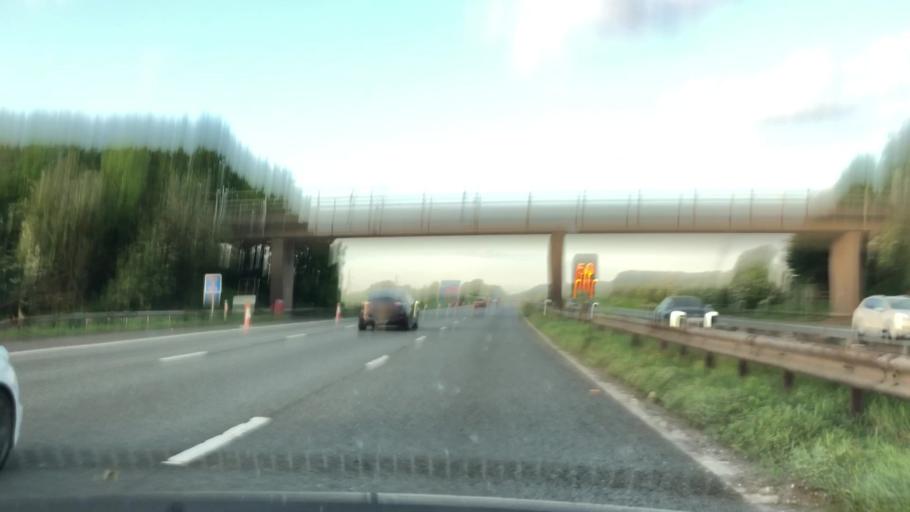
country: GB
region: England
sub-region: Cheshire West and Chester
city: Elton
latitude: 53.2620
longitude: -2.8185
